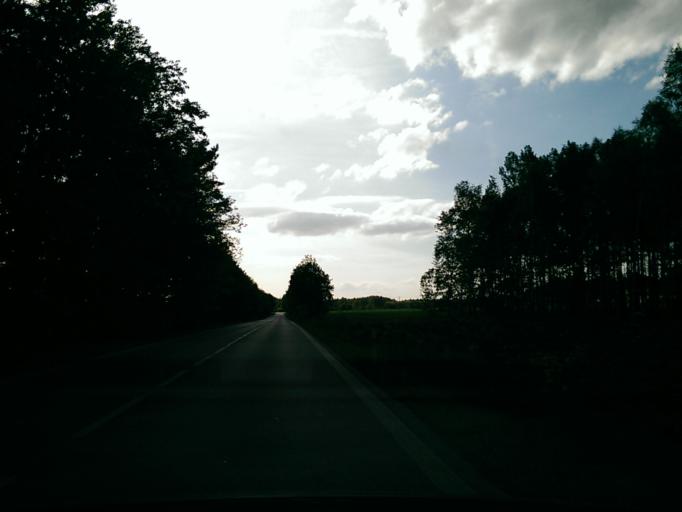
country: CZ
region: Central Bohemia
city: Bela pod Bezdezem
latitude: 50.5191
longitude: 14.7354
